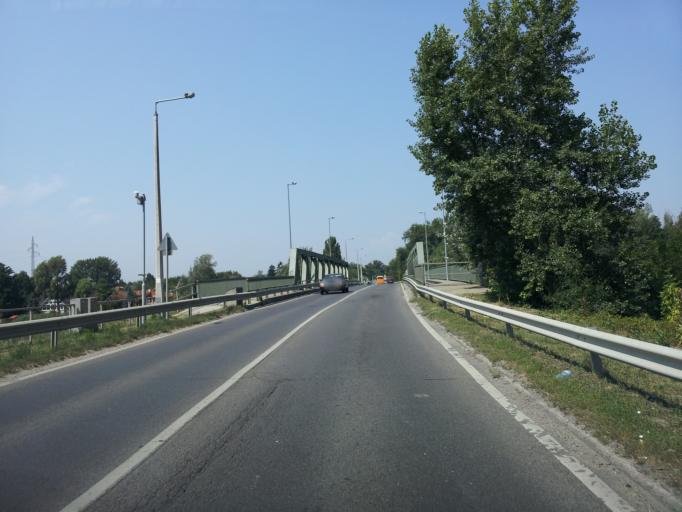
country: HU
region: Pest
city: Szigetszentmiklos
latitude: 47.3119
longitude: 19.0358
